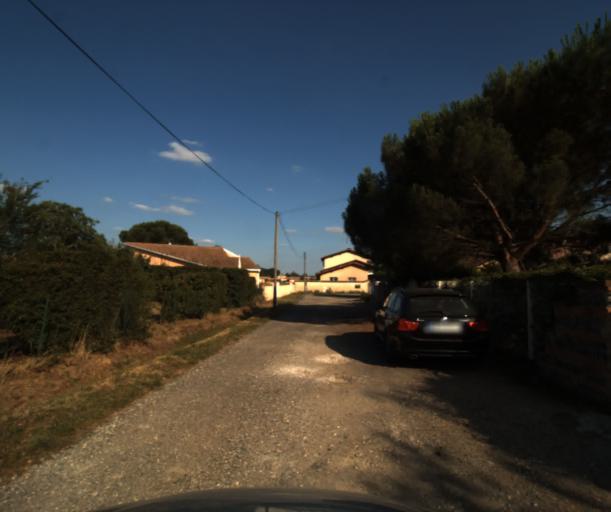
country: FR
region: Midi-Pyrenees
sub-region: Departement de la Haute-Garonne
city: Saint-Lys
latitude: 43.5077
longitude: 1.1920
